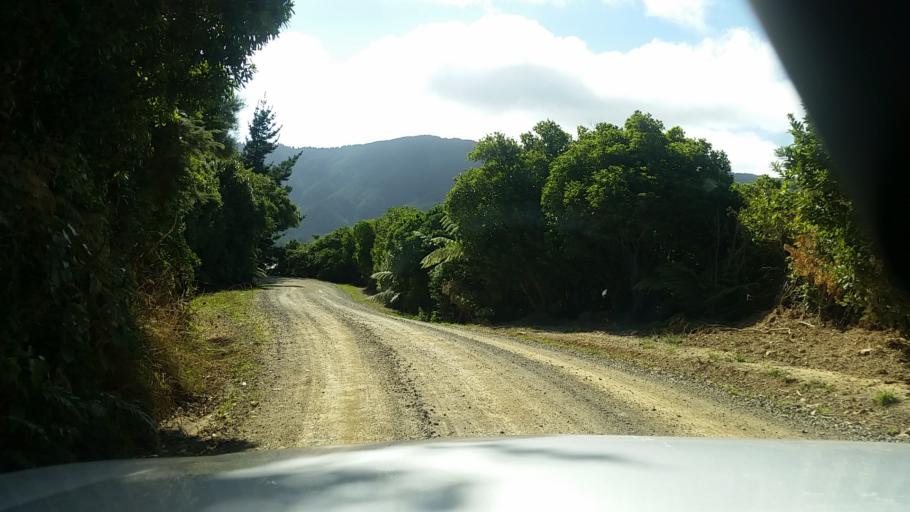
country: NZ
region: Marlborough
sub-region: Marlborough District
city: Picton
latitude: -41.2906
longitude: 174.1702
